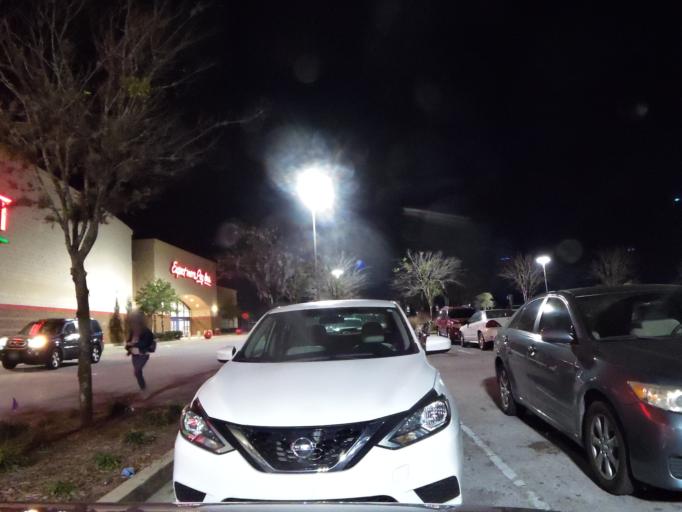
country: US
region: Florida
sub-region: Clay County
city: Orange Park
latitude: 30.2354
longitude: -81.6952
